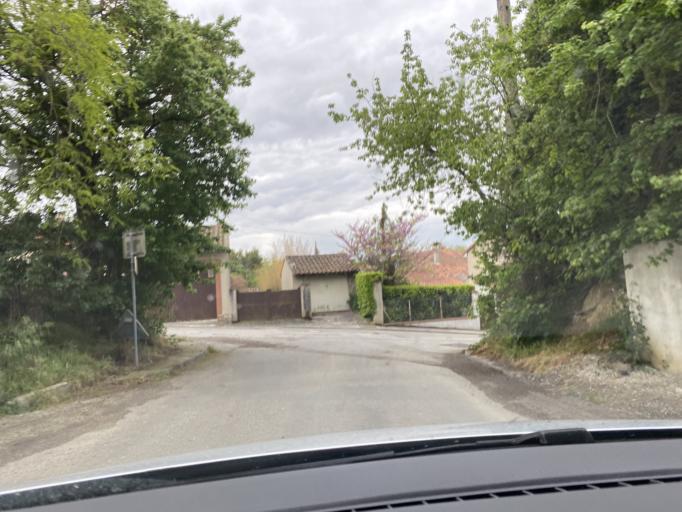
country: FR
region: Midi-Pyrenees
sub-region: Departement de la Haute-Garonne
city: Nailloux
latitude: 43.3601
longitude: 1.6245
